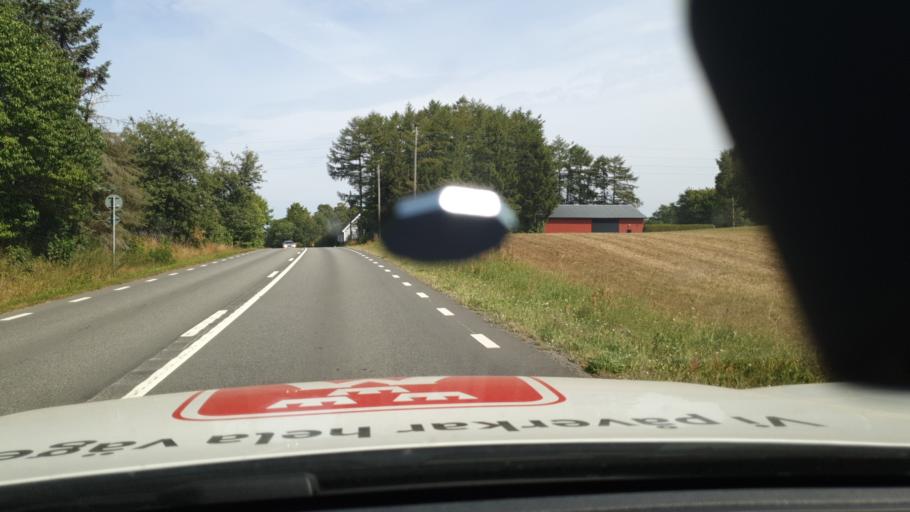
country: SE
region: Skane
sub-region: Simrishamns Kommun
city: Kivik
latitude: 55.6002
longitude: 14.1372
